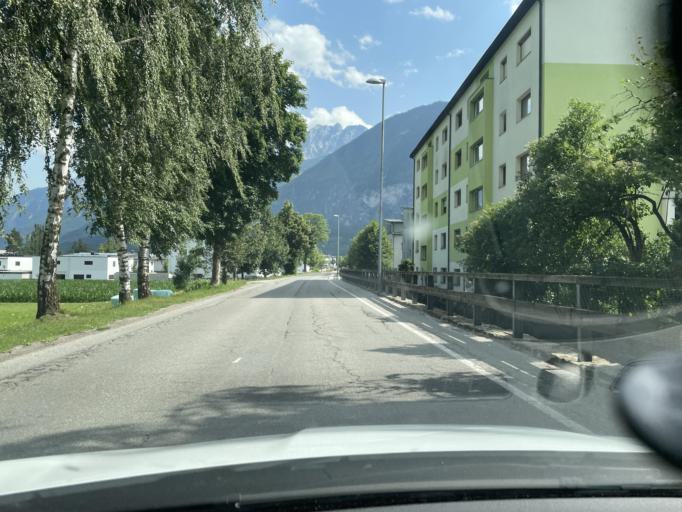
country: AT
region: Tyrol
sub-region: Politischer Bezirk Lienz
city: Lienz
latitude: 46.8348
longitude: 12.7773
